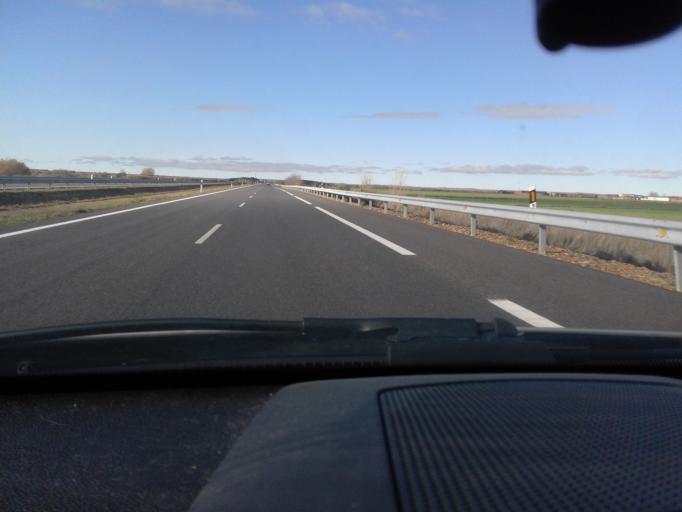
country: ES
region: Castille and Leon
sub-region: Provincia de Palencia
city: Bustillo del Paramo de Carrion
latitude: 42.3494
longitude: -4.7309
